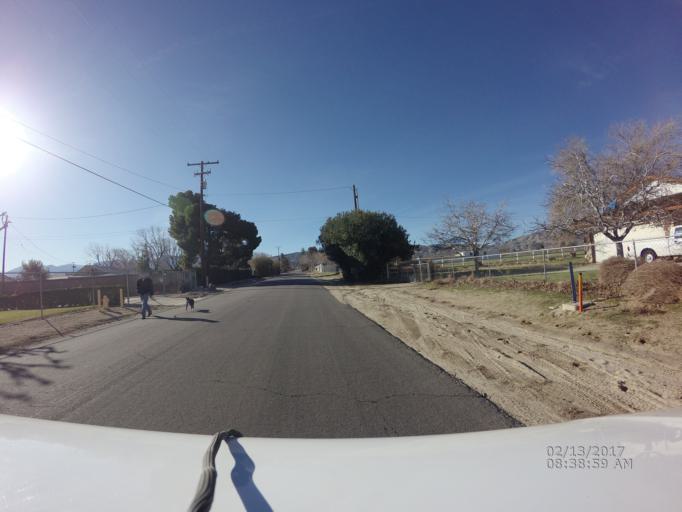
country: US
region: California
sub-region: Los Angeles County
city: Littlerock
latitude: 34.5267
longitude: -117.9882
